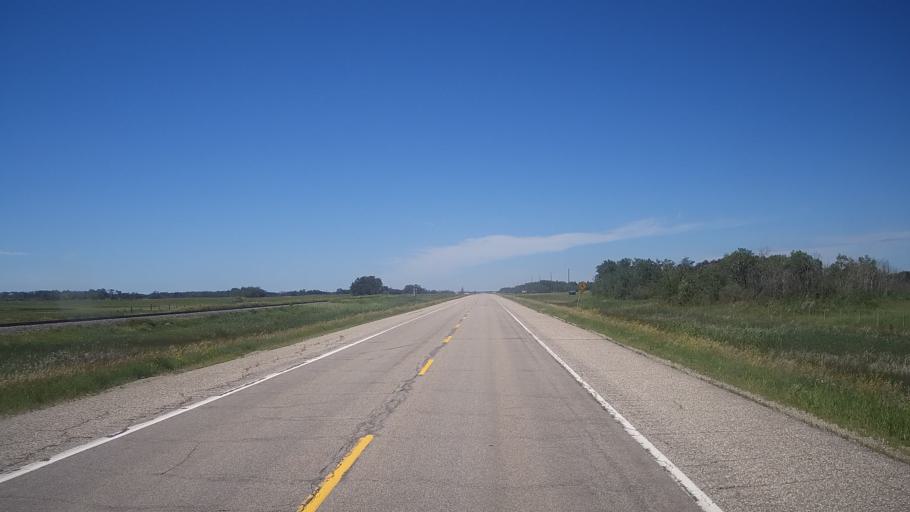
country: CA
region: Manitoba
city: Rivers
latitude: 50.4247
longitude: -100.5092
